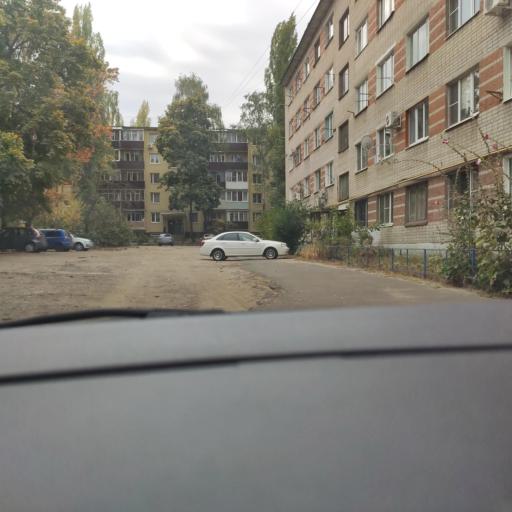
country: RU
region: Voronezj
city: Voronezh
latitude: 51.6504
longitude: 39.1286
